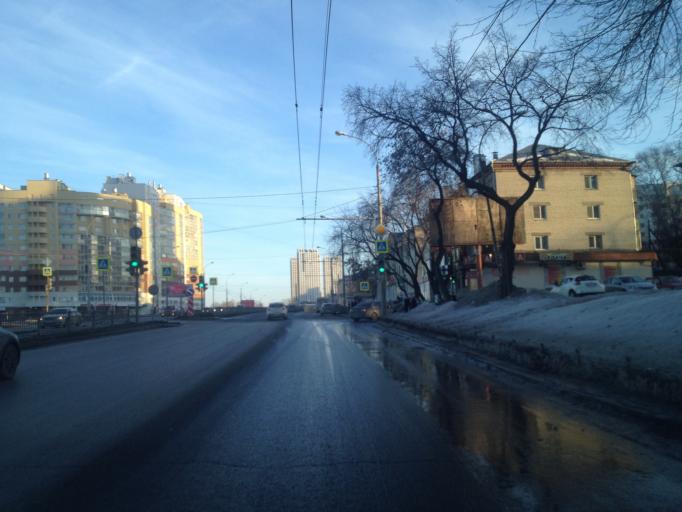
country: RU
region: Sverdlovsk
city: Yekaterinburg
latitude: 56.7842
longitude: 60.6517
